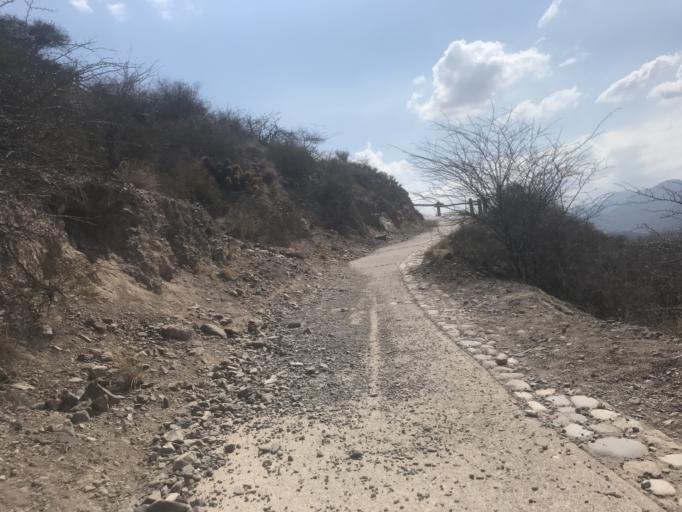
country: AR
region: Mendoza
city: Mendoza
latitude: -32.8855
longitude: -68.8894
